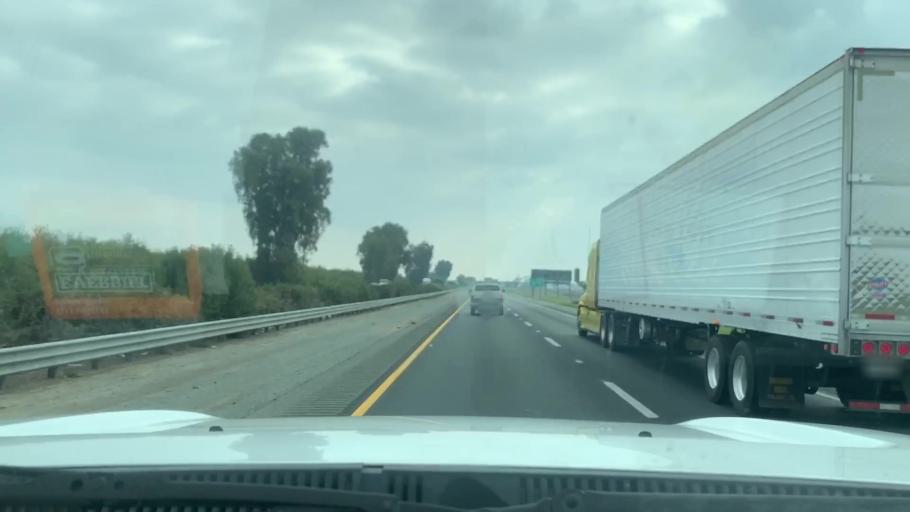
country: US
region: California
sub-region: Tulare County
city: Tipton
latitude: 36.0180
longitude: -119.3049
